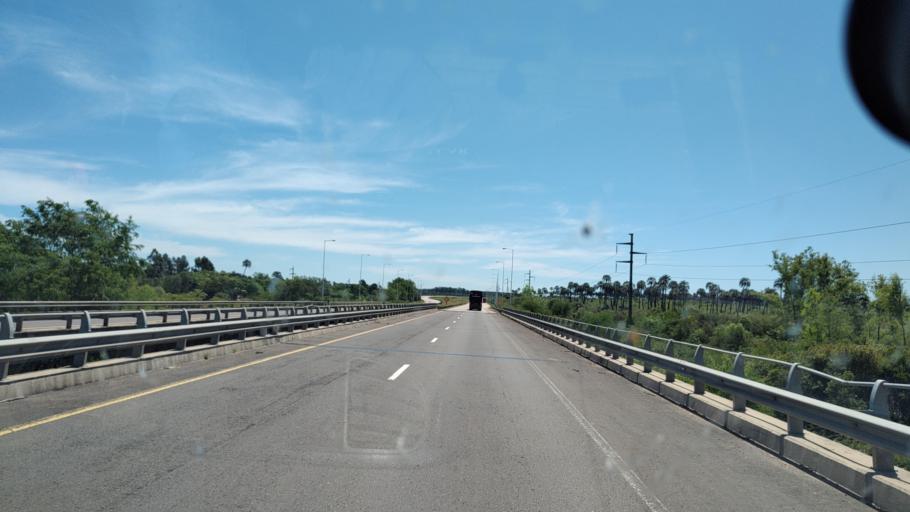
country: AR
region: Entre Rios
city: Ubajay
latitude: -31.8613
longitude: -58.3234
